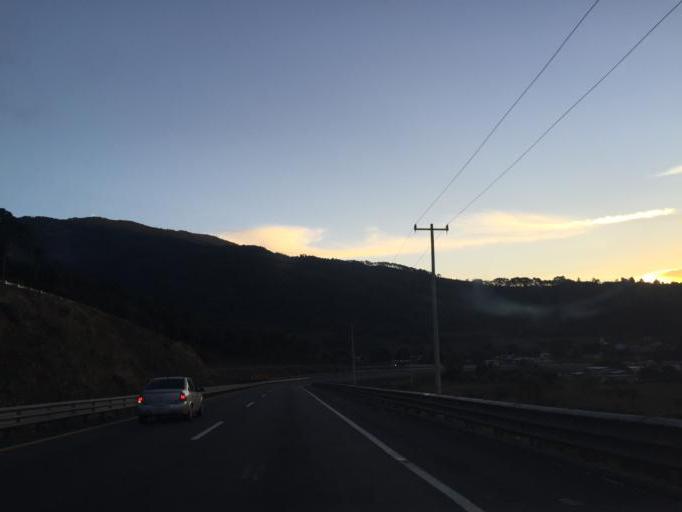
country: MX
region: Veracruz
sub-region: Maltrata
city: San Jose Suchil
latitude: 18.8522
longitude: -97.2608
